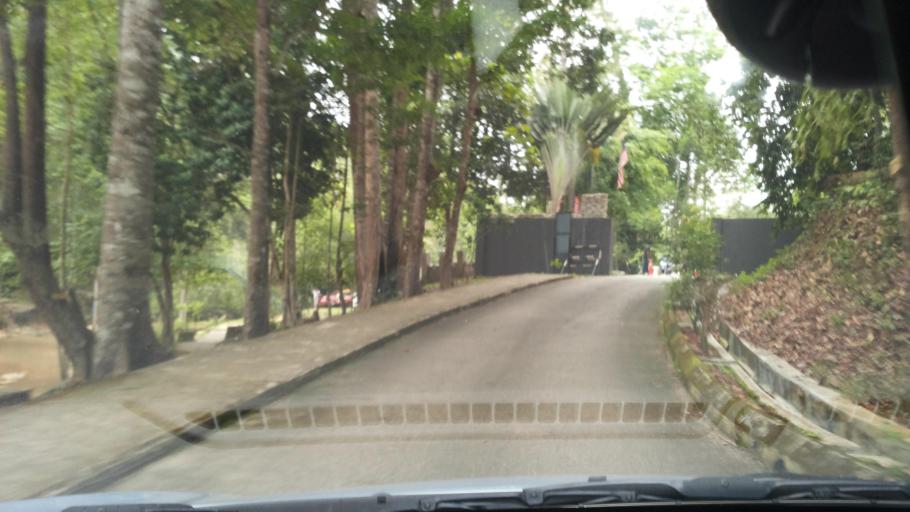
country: MY
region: Pahang
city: Kuantan
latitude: 3.7906
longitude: 103.1442
